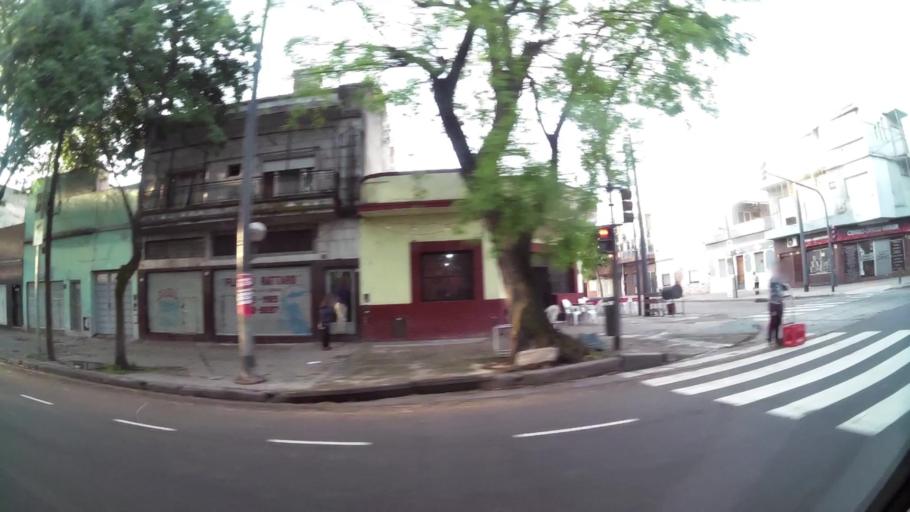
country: AR
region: Buenos Aires F.D.
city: Villa Lugano
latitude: -34.6425
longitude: -58.4363
